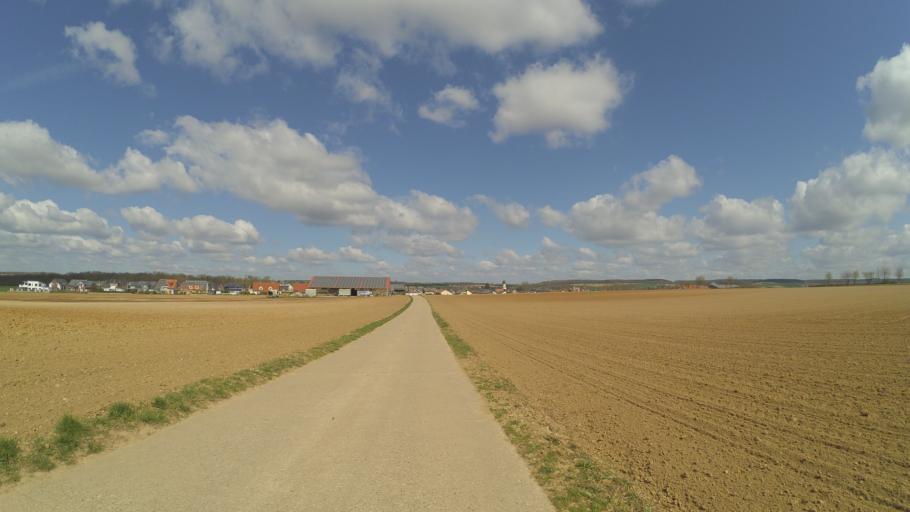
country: DE
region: Baden-Wuerttemberg
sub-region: Regierungsbezirk Stuttgart
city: Oedheim
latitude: 49.2441
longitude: 9.2869
